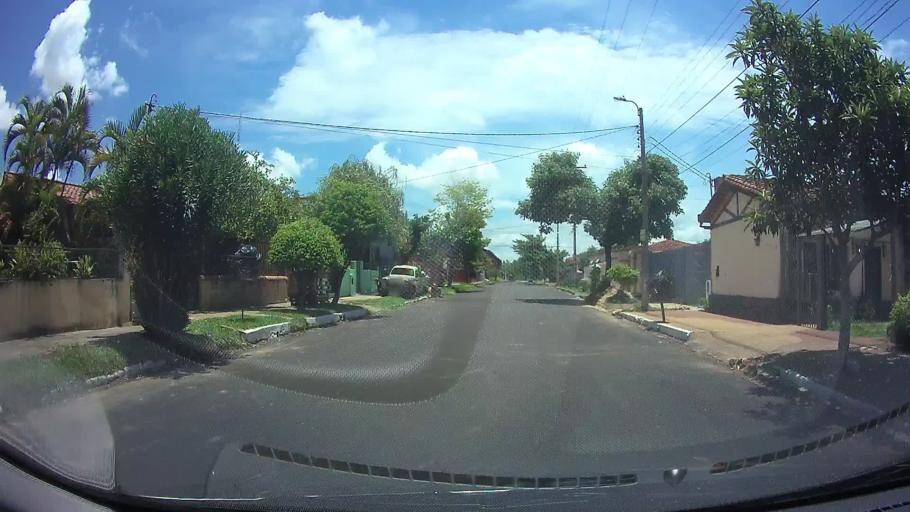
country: PY
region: Central
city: San Lorenzo
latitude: -25.2638
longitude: -57.5006
